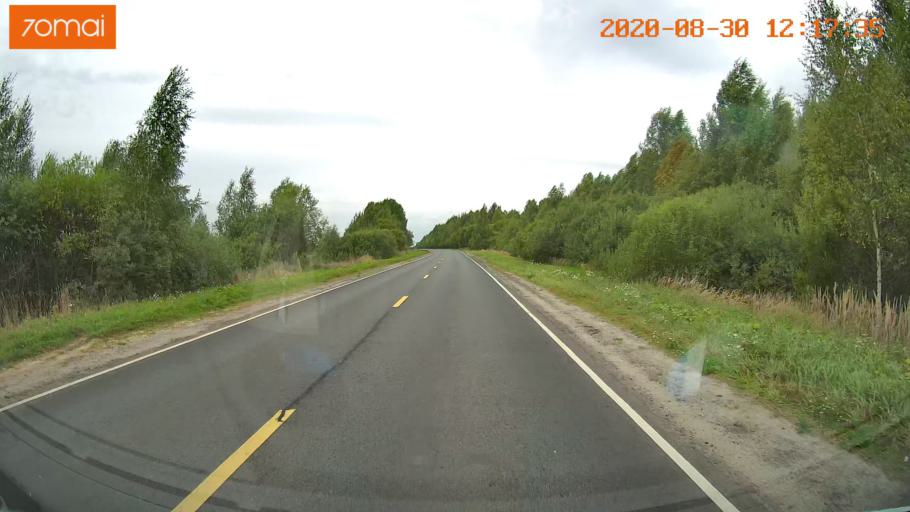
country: RU
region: Ivanovo
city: Yur'yevets
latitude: 57.3236
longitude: 42.9741
